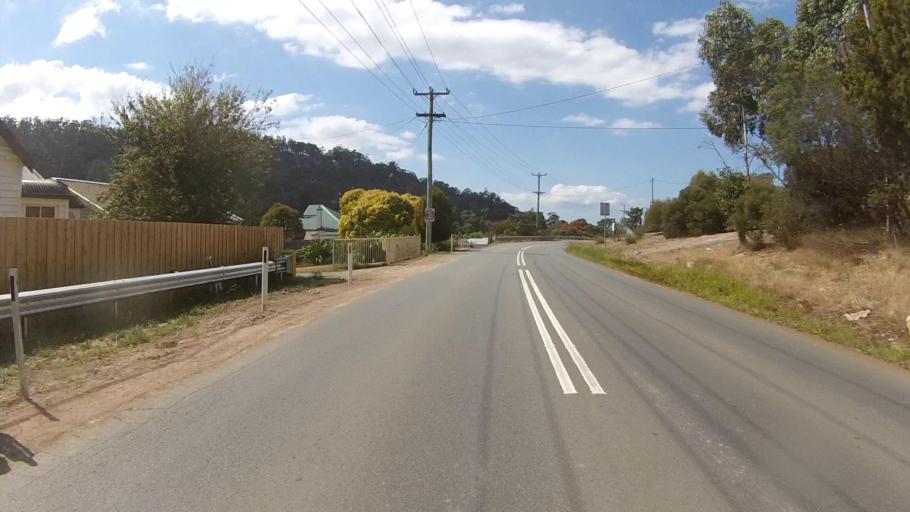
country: AU
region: Tasmania
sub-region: Clarence
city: Cambridge
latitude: -42.8391
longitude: 147.4252
